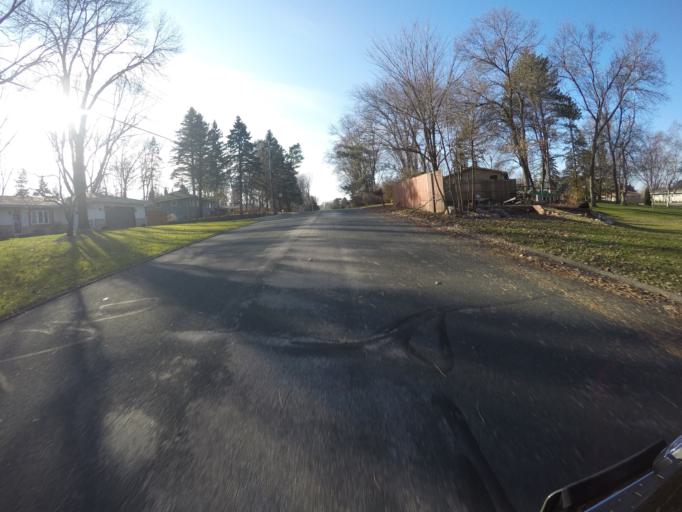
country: US
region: Minnesota
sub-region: Hennepin County
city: Eden Prairie
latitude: 44.8766
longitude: -93.4903
